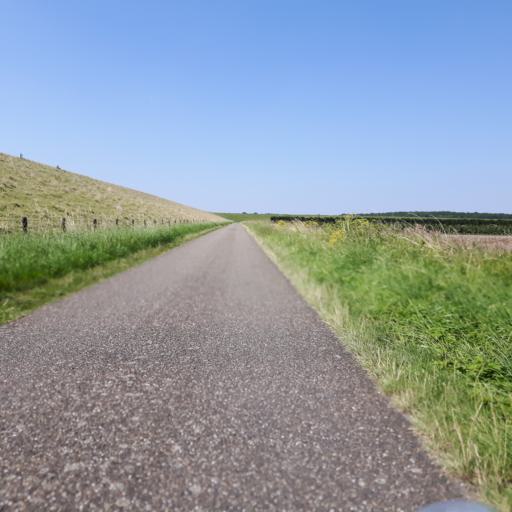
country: NL
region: Zeeland
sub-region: Gemeente Reimerswaal
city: Yerseke
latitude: 51.4229
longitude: 4.0522
